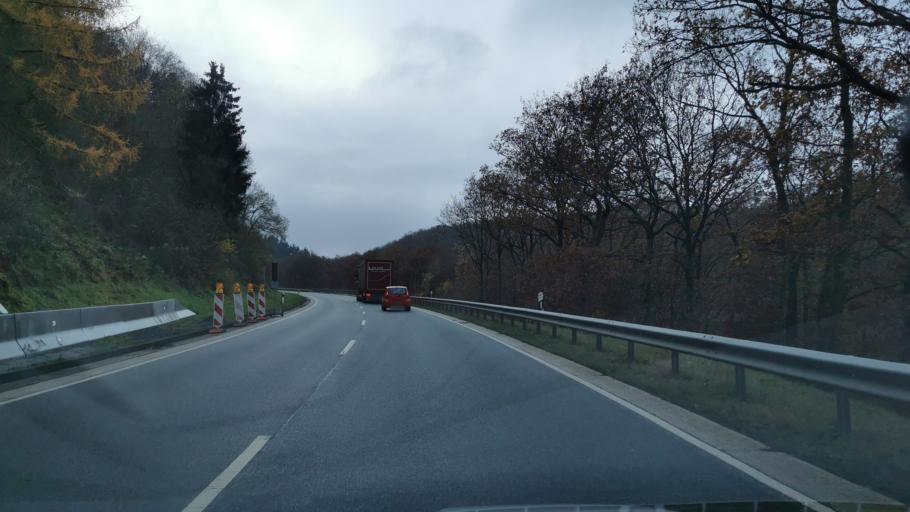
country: DE
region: Rheinland-Pfalz
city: Cochem
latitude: 50.1385
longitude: 7.1550
